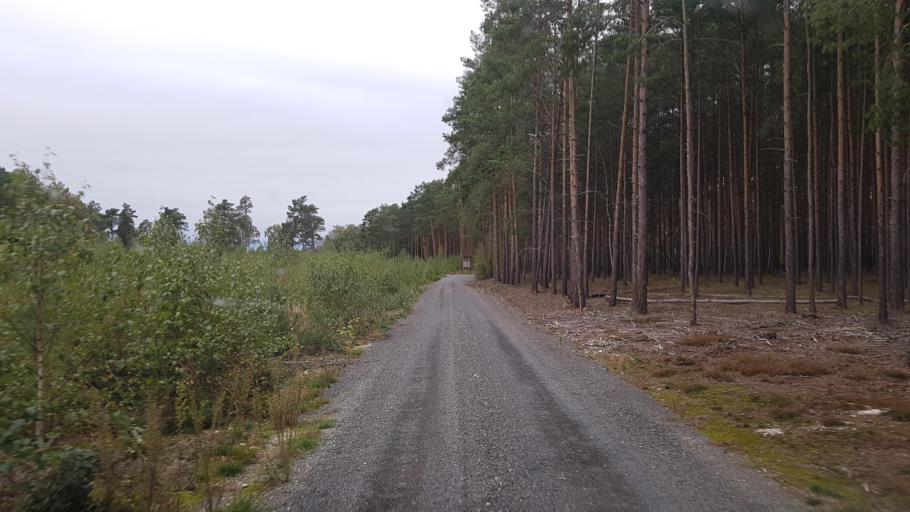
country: DE
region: Brandenburg
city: Sonnewalde
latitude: 51.7221
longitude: 13.6668
